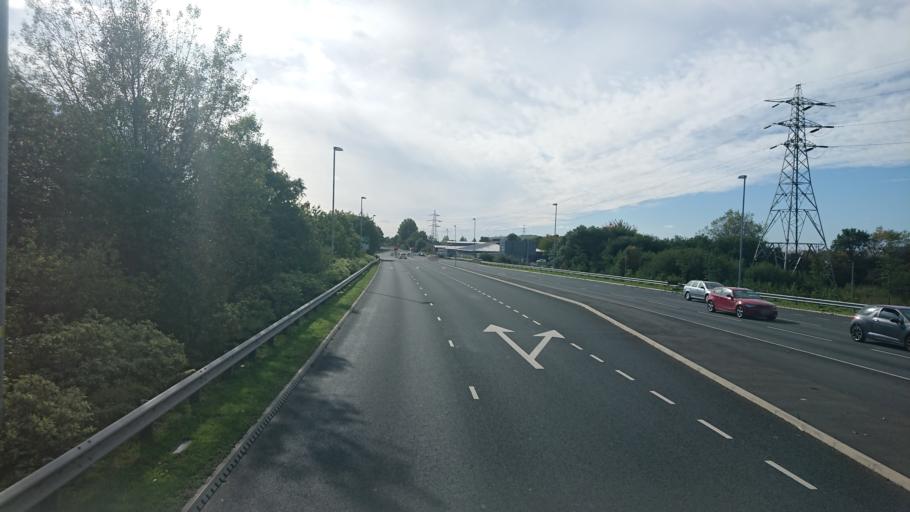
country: GB
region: England
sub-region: Lancashire
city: Morecambe
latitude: 54.0605
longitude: -2.8323
